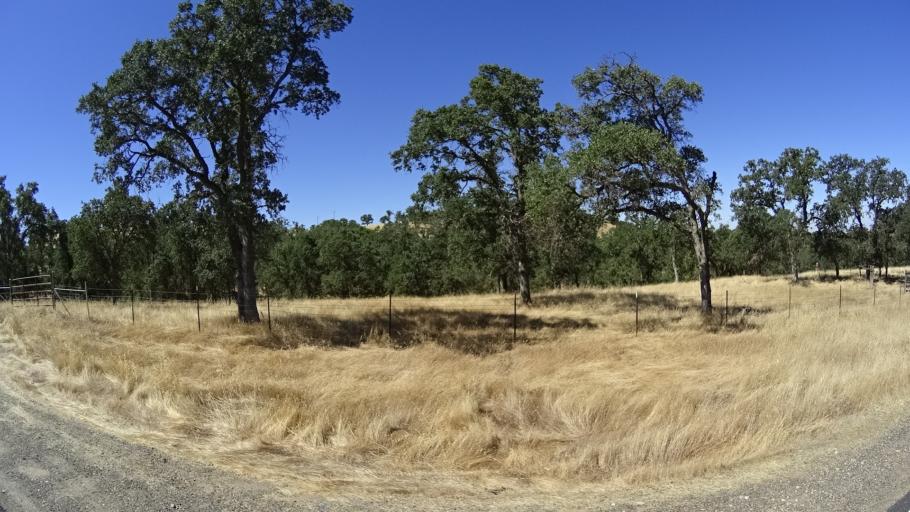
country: US
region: California
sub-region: Calaveras County
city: Rancho Calaveras
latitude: 38.0709
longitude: -120.8667
